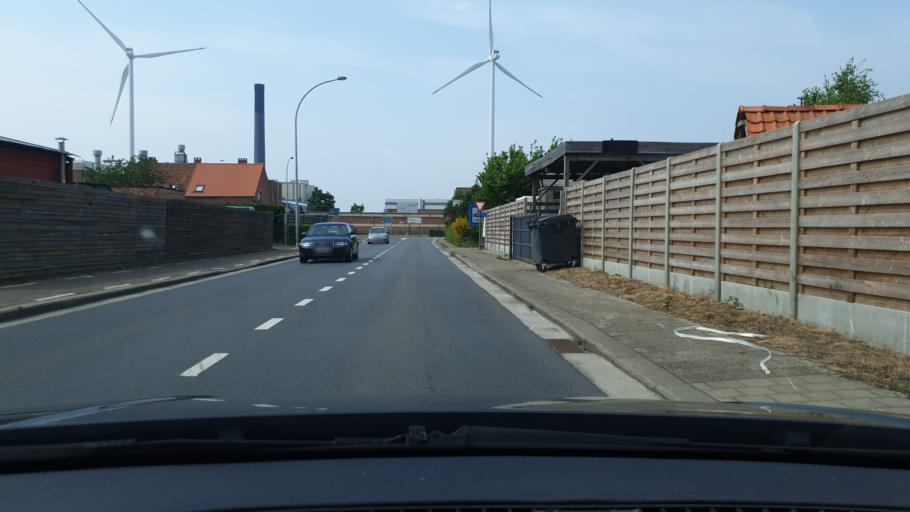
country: BE
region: Flanders
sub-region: Provincie Antwerpen
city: Olen
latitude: 51.1782
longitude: 4.8896
